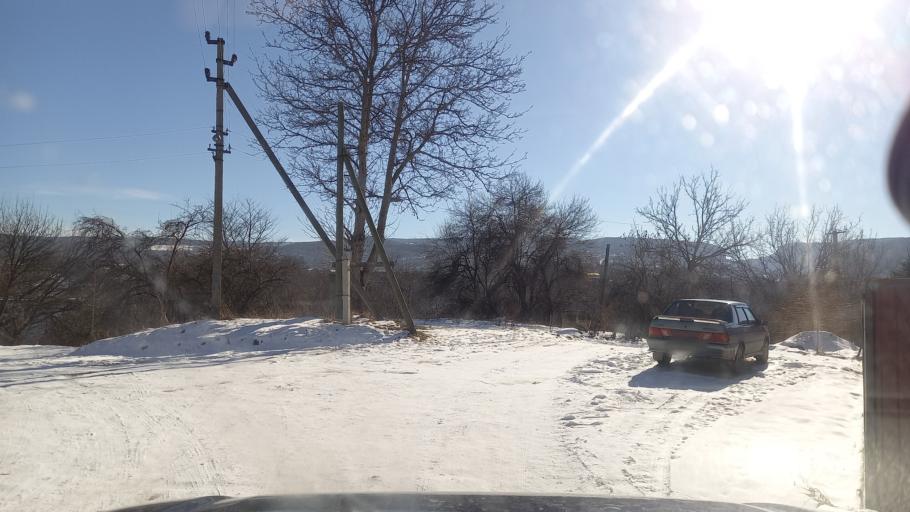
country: RU
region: Adygeya
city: Kamennomostskiy
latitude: 44.2979
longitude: 40.1718
